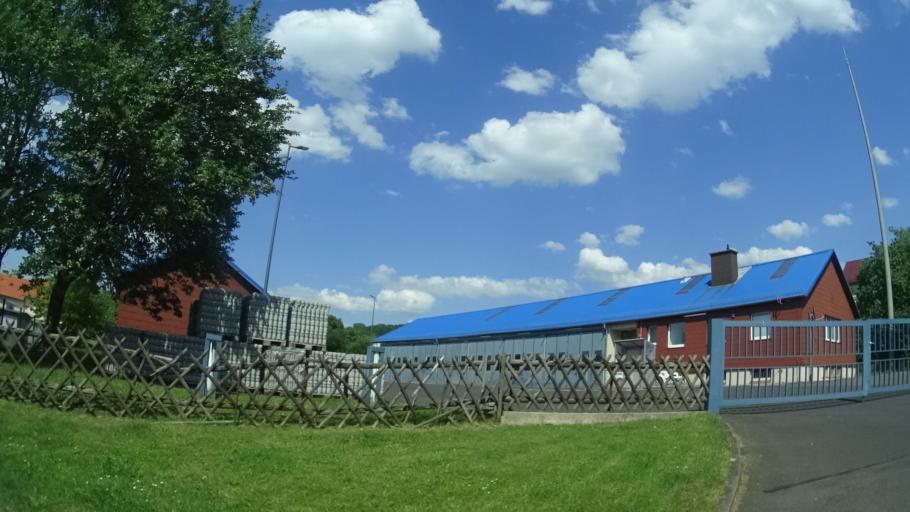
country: DE
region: Hesse
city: Tann
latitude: 50.6377
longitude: 10.0224
